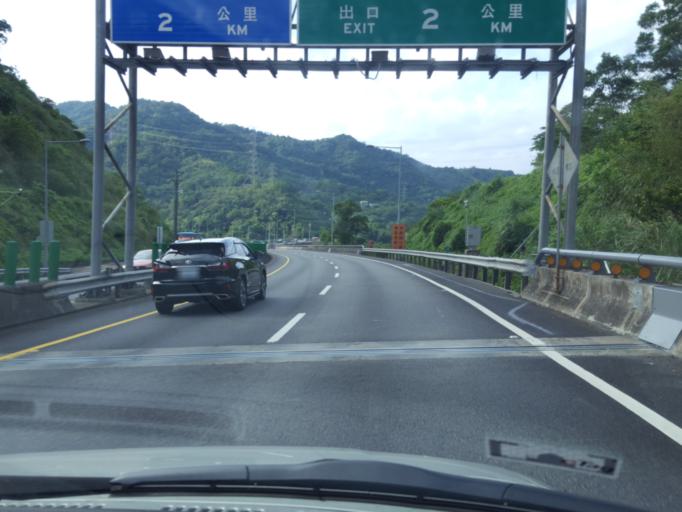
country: TW
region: Taipei
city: Taipei
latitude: 24.9894
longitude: 121.6581
